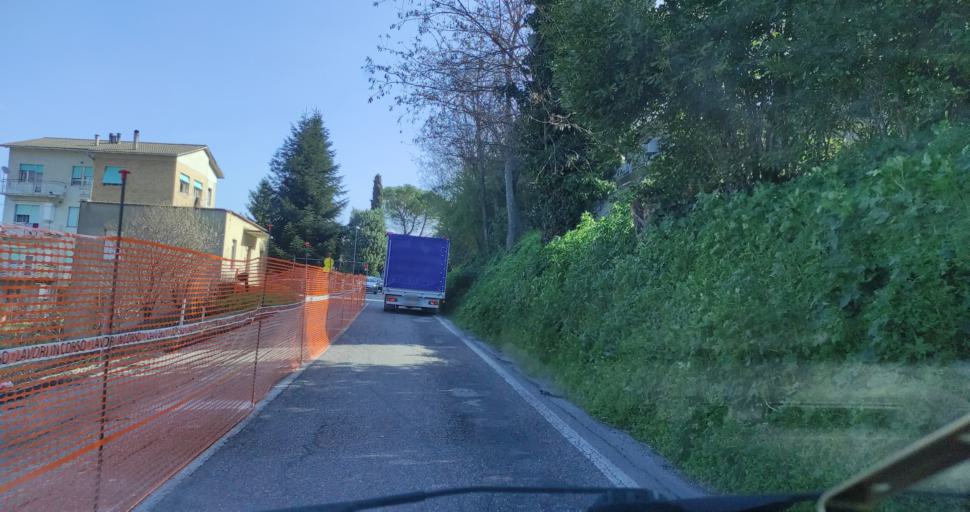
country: IT
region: The Marches
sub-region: Provincia di Macerata
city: Corridonia
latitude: 43.2504
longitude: 13.5032
